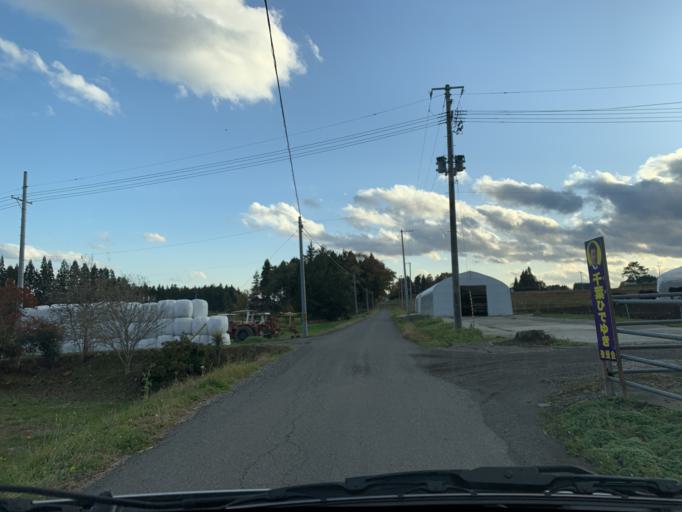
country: JP
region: Iwate
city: Mizusawa
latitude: 39.1056
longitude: 141.0396
